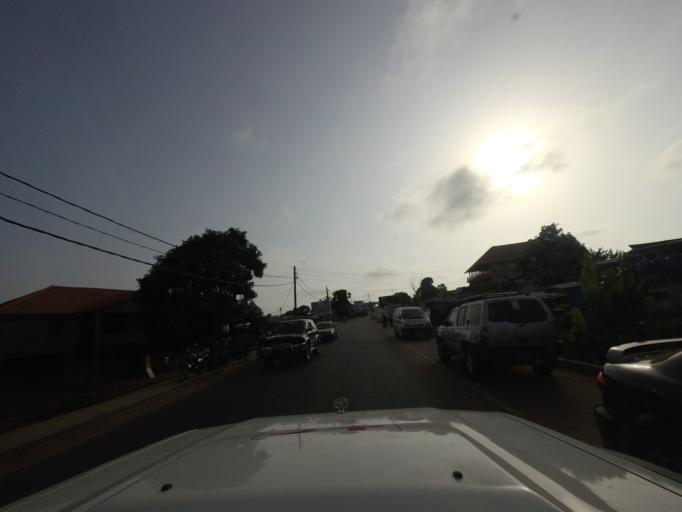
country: SL
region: Western Area
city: Freetown
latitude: 8.4917
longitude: -13.2825
